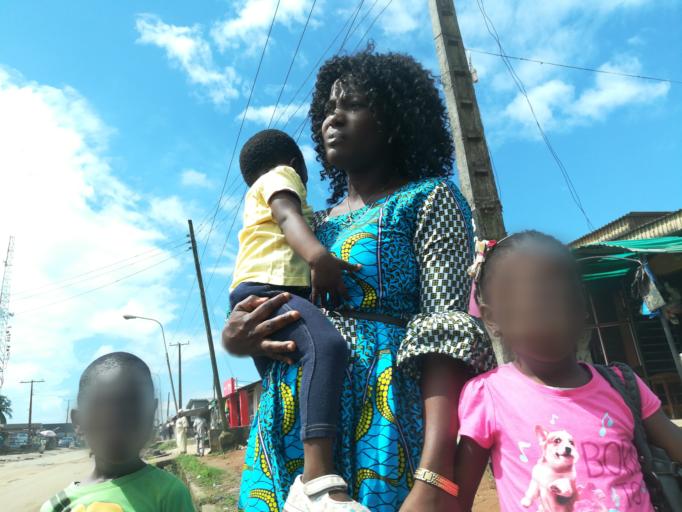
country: NG
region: Lagos
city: Ikorodu
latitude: 6.6022
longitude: 3.5182
